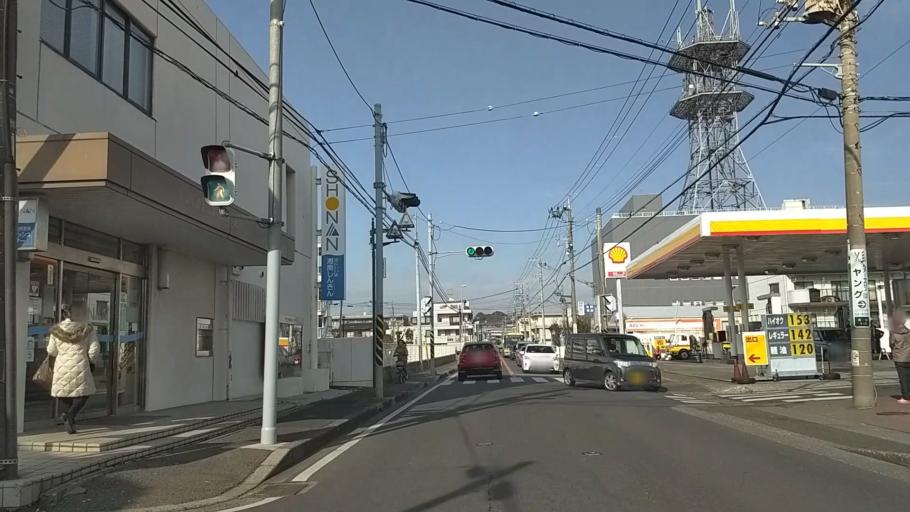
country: JP
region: Kanagawa
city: Chigasaki
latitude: 35.3457
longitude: 139.4129
